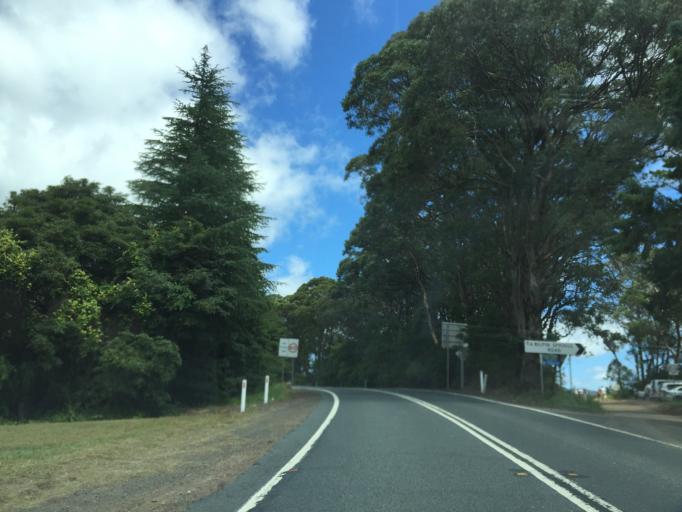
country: AU
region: New South Wales
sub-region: Blue Mountains Municipality
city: Hazelbrook
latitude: -33.4971
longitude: 150.5142
